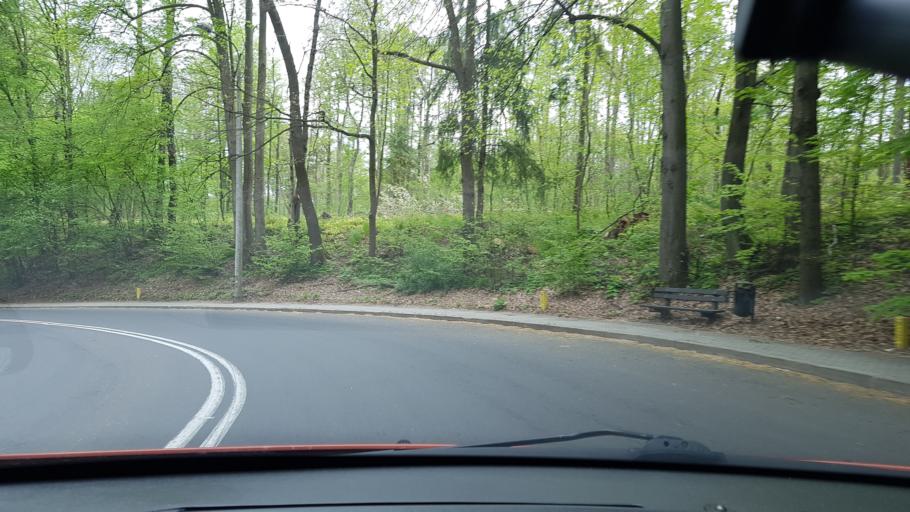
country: PL
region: Opole Voivodeship
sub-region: Powiat nyski
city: Glucholazy
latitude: 50.3128
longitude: 17.3515
